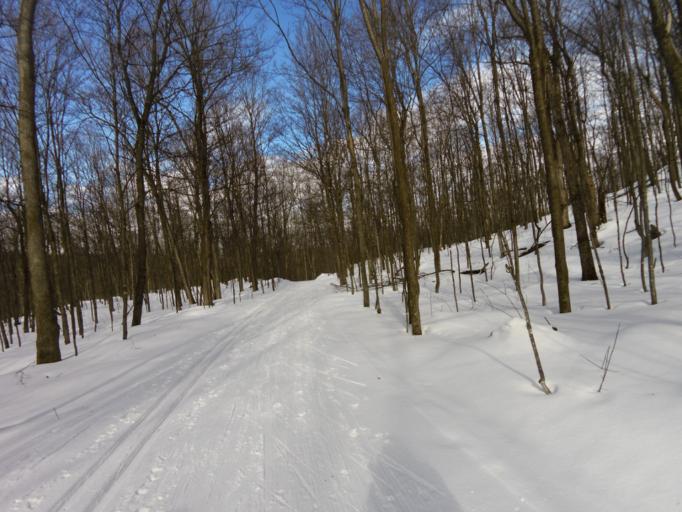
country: CA
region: Quebec
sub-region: Outaouais
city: Wakefield
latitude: 45.5310
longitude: -75.9019
